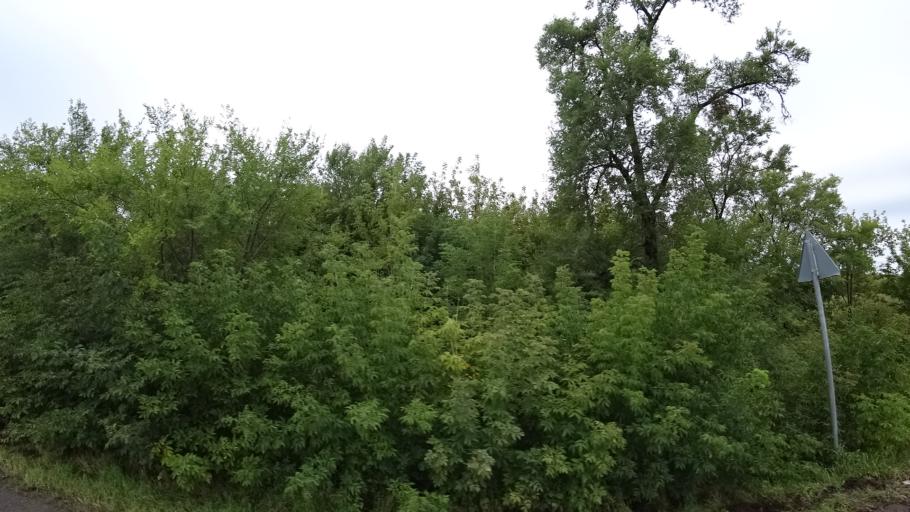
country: RU
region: Primorskiy
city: Monastyrishche
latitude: 44.1927
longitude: 132.4807
